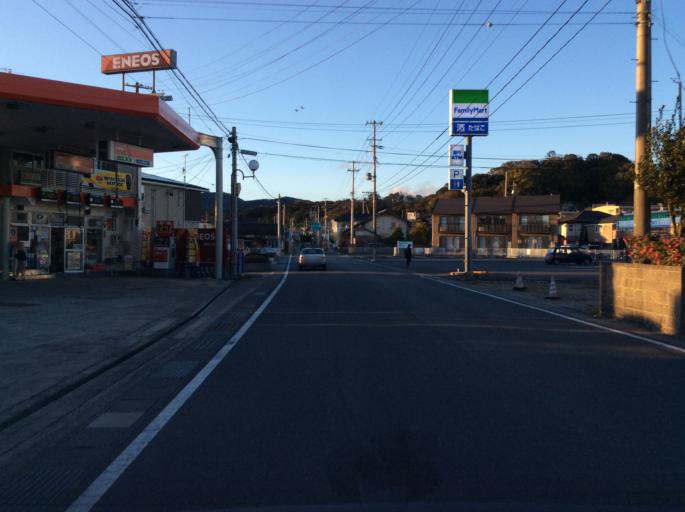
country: JP
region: Fukushima
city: Iwaki
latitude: 37.0847
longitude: 140.8652
